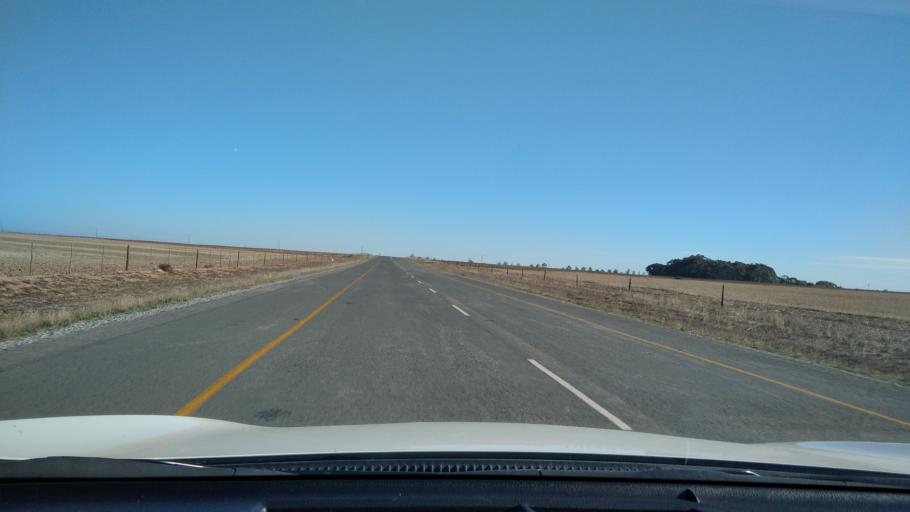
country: ZA
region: Western Cape
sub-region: West Coast District Municipality
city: Malmesbury
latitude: -33.3298
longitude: 18.6305
